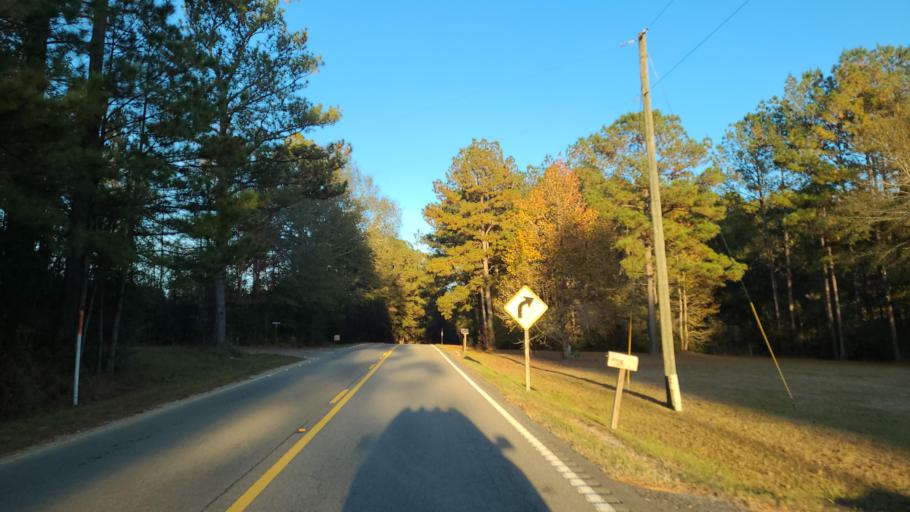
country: US
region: Mississippi
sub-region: Lamar County
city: Lumberton
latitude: 31.0006
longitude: -89.3556
